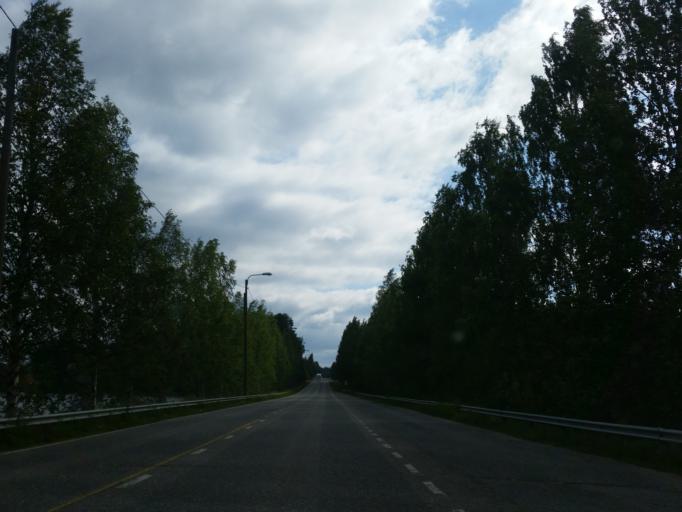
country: FI
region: Northern Savo
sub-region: Sisae-Savo
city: Tervo
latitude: 62.9536
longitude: 26.7461
